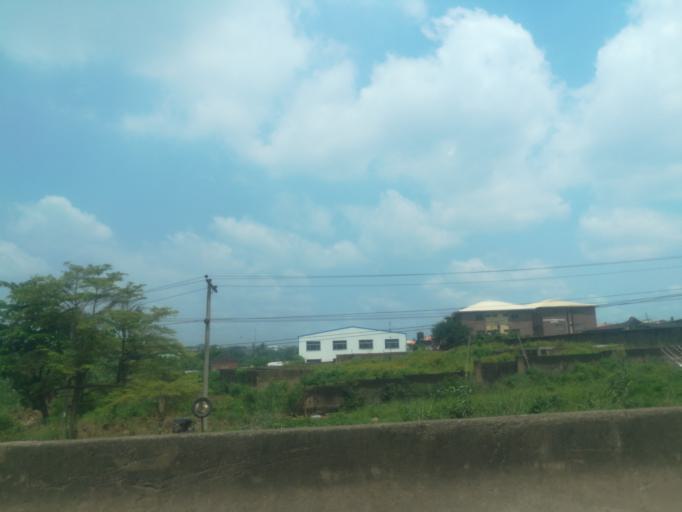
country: NG
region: Oyo
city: Ibadan
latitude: 7.3945
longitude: 3.9554
